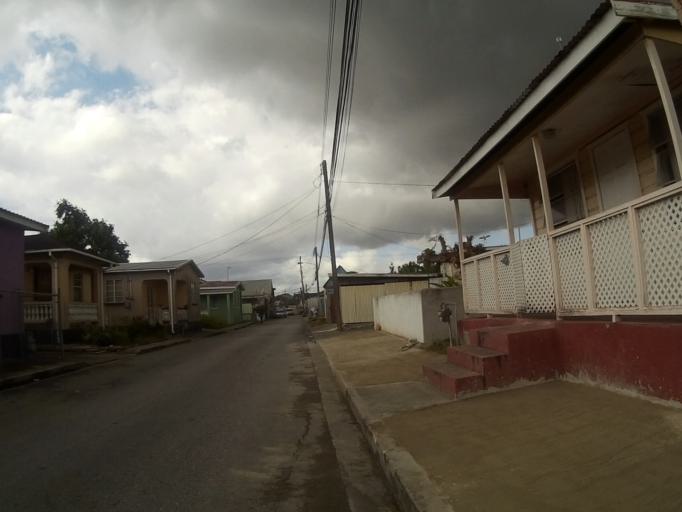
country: BB
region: Saint Michael
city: Bridgetown
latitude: 13.1019
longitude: -59.6039
